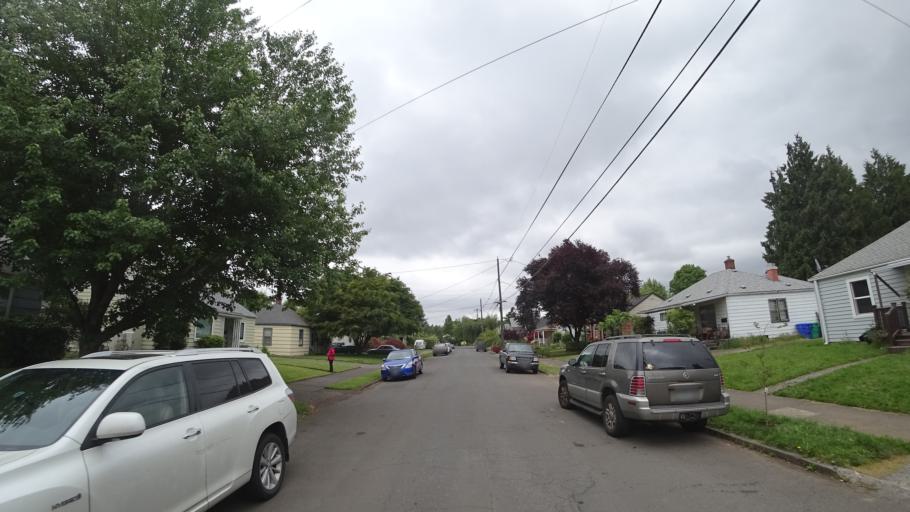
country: US
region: Oregon
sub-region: Clackamas County
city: Milwaukie
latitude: 45.4889
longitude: -122.6159
